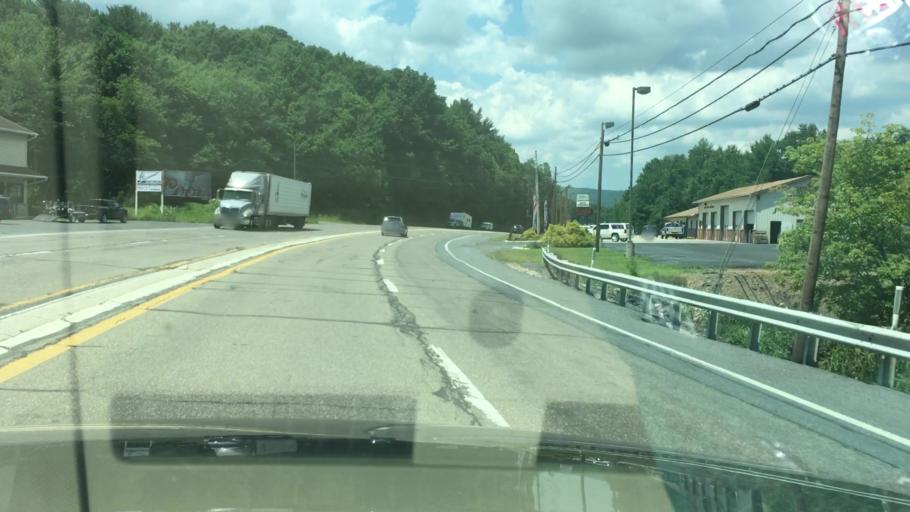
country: US
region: Pennsylvania
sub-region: Schuylkill County
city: Minersville
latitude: 40.6740
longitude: -76.2440
